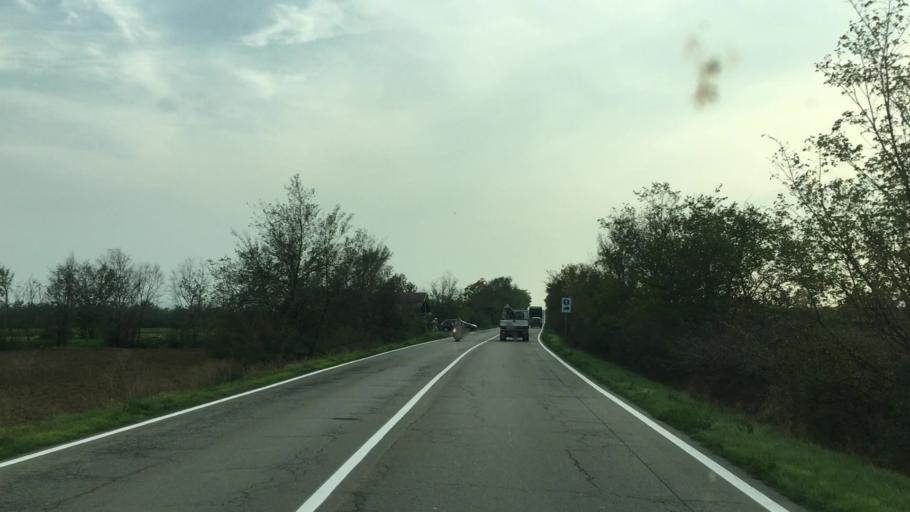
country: IT
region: Emilia-Romagna
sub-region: Provincia di Reggio Emilia
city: Calerno
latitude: 44.7551
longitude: 10.4954
